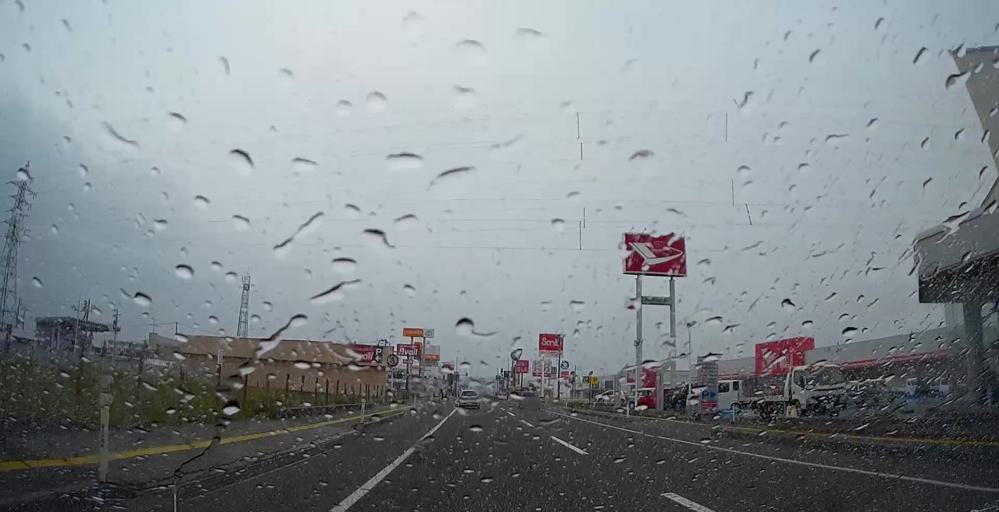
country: JP
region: Niigata
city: Kashiwazaki
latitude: 37.3767
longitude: 138.5800
